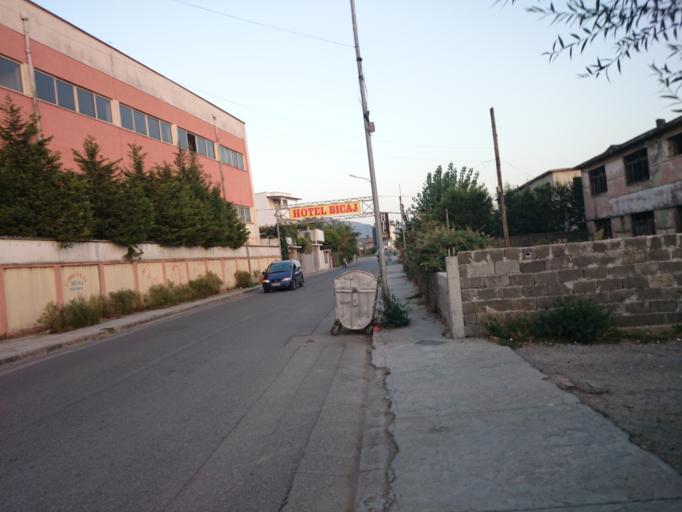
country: AL
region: Shkoder
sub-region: Rrethi i Shkodres
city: Shkoder
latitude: 42.0595
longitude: 19.5230
